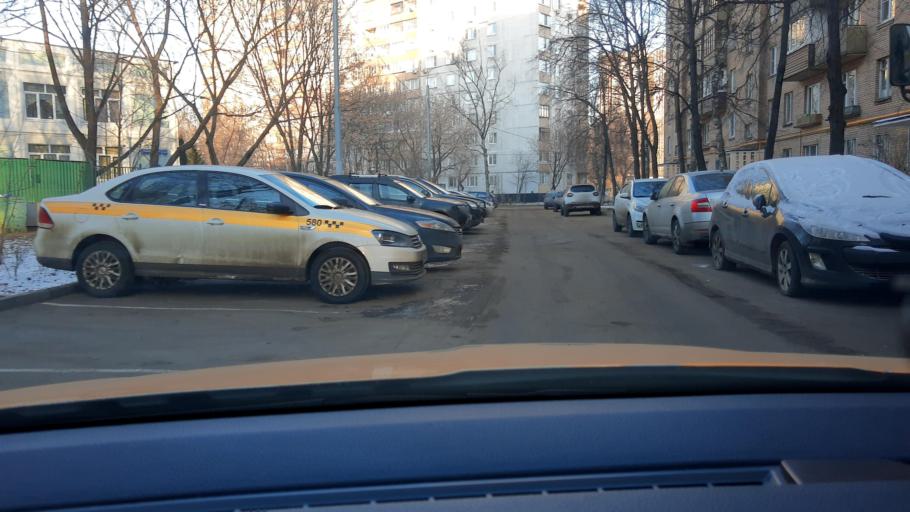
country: RU
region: Moscow
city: Lyublino
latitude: 55.6669
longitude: 37.7458
